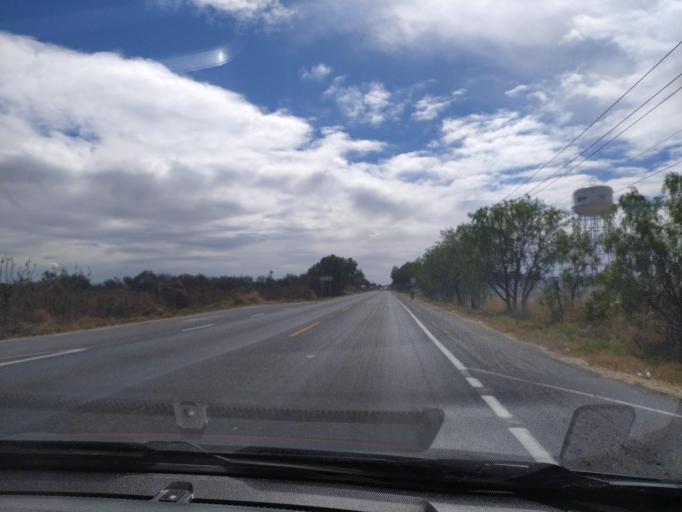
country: LA
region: Oudomxai
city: Muang La
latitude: 21.0242
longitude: 101.8257
